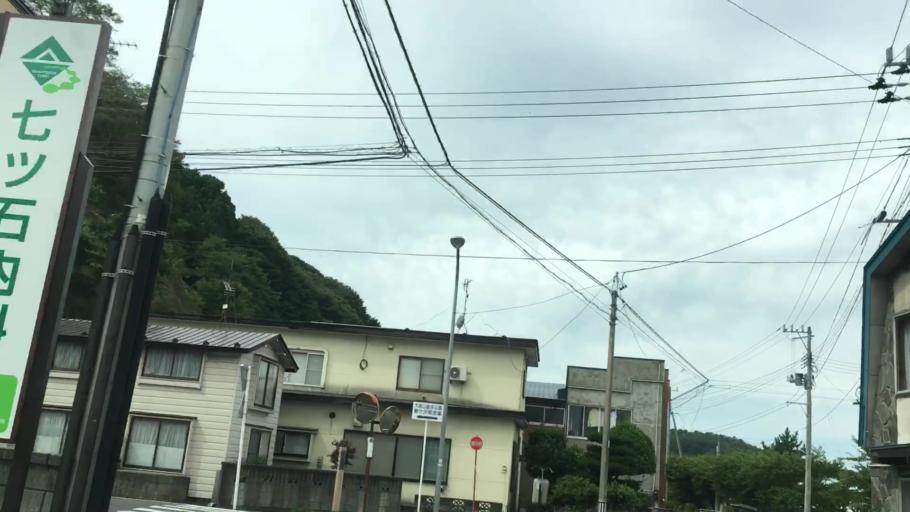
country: JP
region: Aomori
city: Shimokizukuri
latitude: 40.7780
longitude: 140.2131
